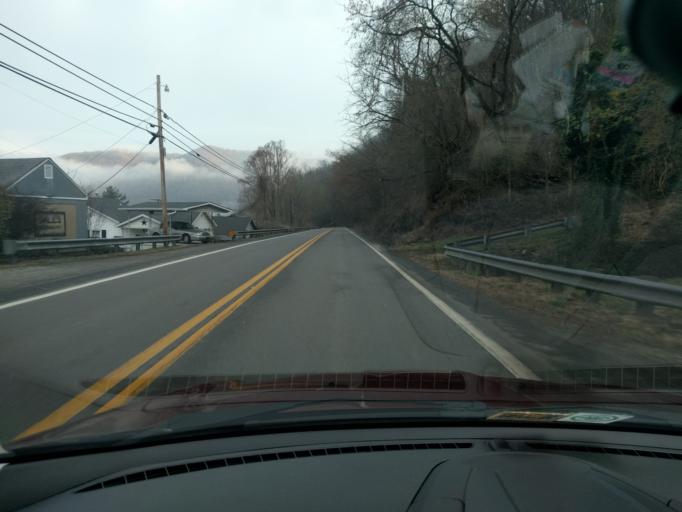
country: US
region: West Virginia
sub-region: Kanawha County
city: Montgomery
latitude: 38.1679
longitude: -81.3029
